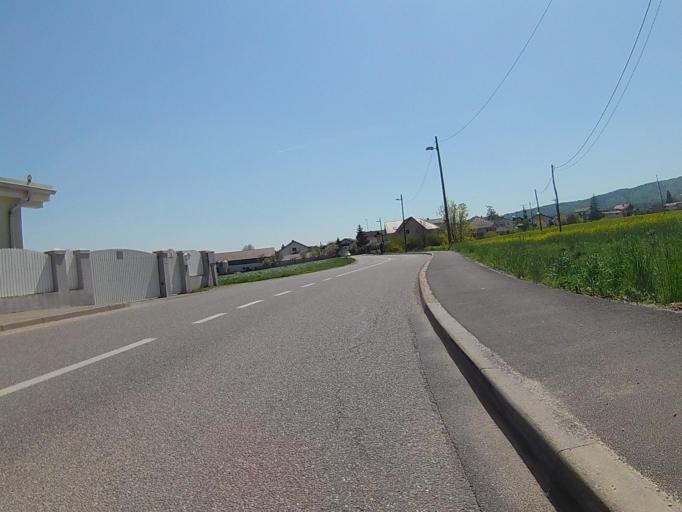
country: SI
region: Hoce-Slivnica
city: Spodnje Hoce
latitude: 46.5046
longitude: 15.6421
